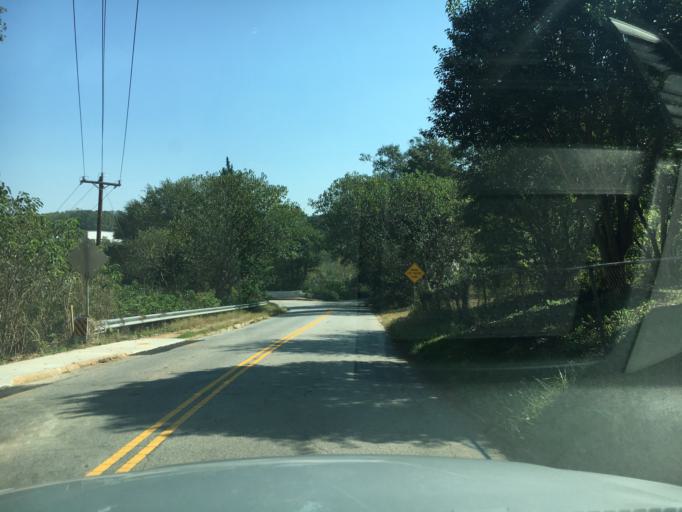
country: US
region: South Carolina
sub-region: Spartanburg County
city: Wellford
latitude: 34.9267
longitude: -82.1016
